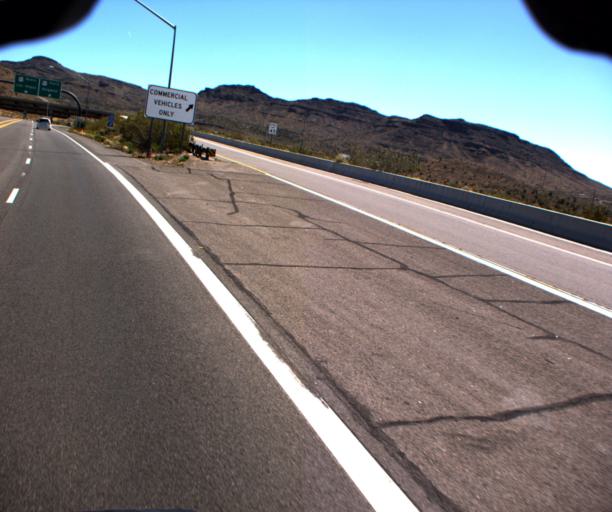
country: US
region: Arizona
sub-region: Mohave County
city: Kingman
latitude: 35.2198
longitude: -114.1300
